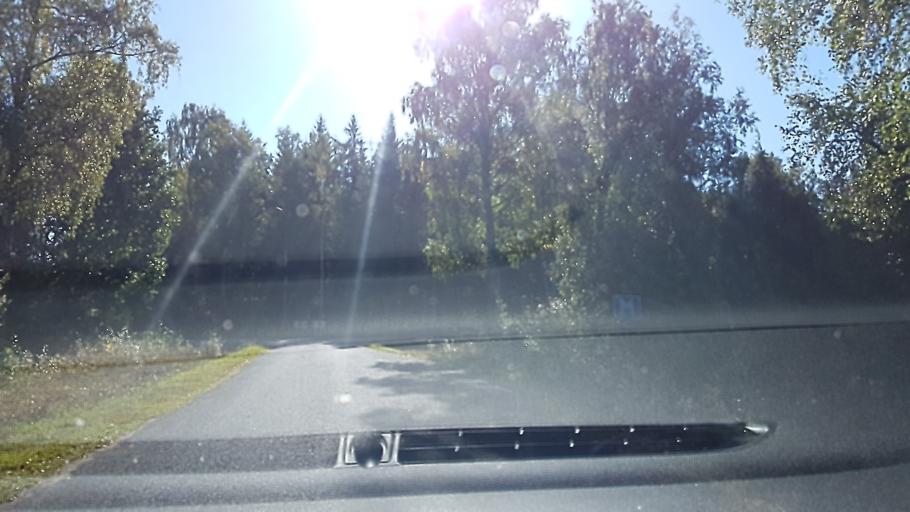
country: SE
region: Kronoberg
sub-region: Ljungby Kommun
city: Ljungby
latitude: 56.8038
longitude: 14.0331
